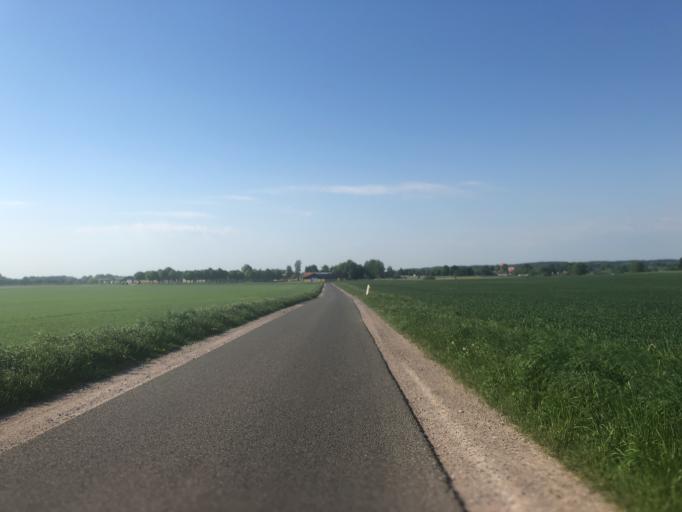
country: DK
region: Zealand
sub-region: Ringsted Kommune
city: Ringsted
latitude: 55.4777
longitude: 11.7695
